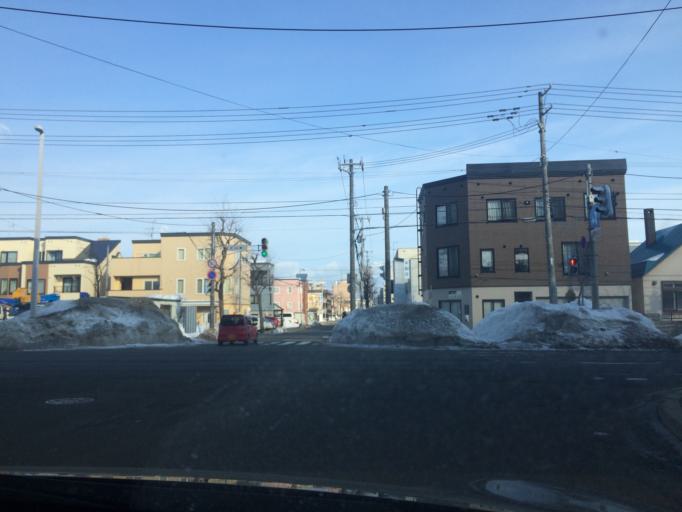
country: JP
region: Hokkaido
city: Sapporo
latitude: 43.1017
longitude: 141.3488
